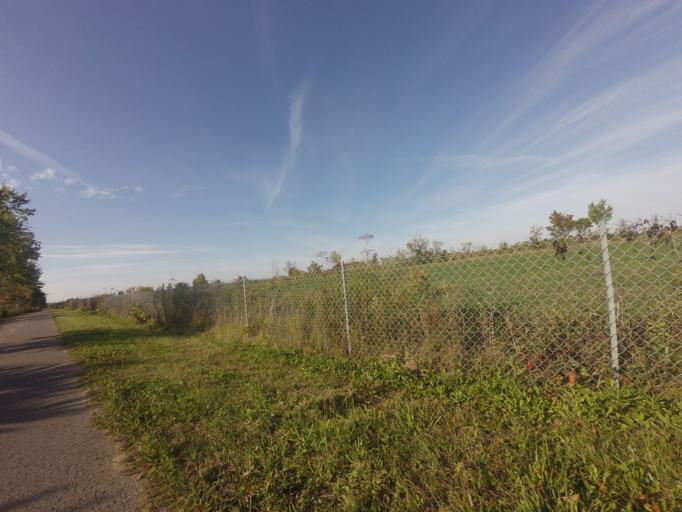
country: CA
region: Quebec
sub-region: Laurentides
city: Blainville
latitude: 45.7168
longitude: -73.9250
